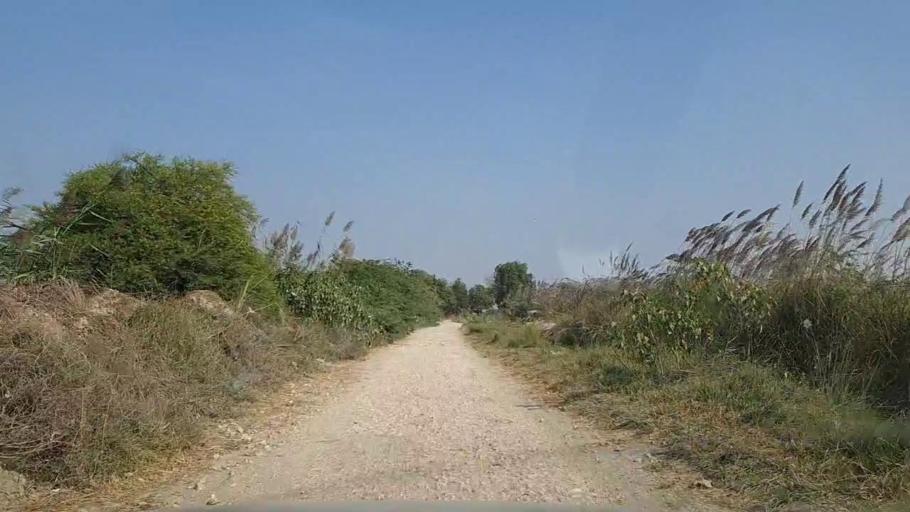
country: PK
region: Sindh
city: Mirpur Sakro
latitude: 24.5583
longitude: 67.5871
